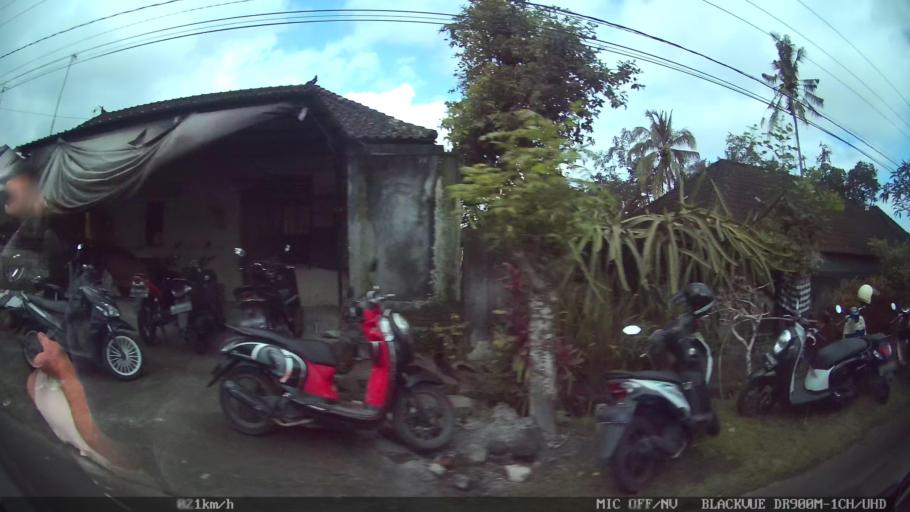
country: ID
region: Bali
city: Banjar Pesalakan
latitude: -8.4867
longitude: 115.3047
